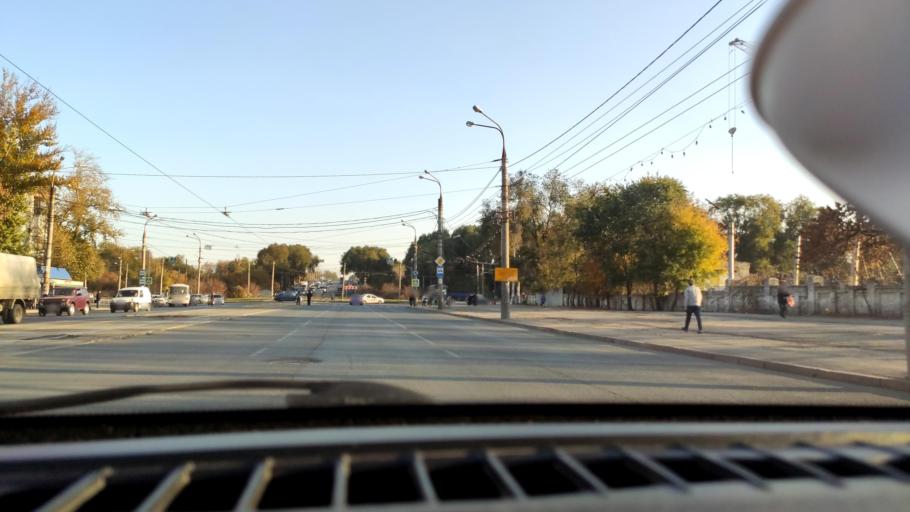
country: RU
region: Samara
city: Samara
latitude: 53.2046
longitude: 50.2376
